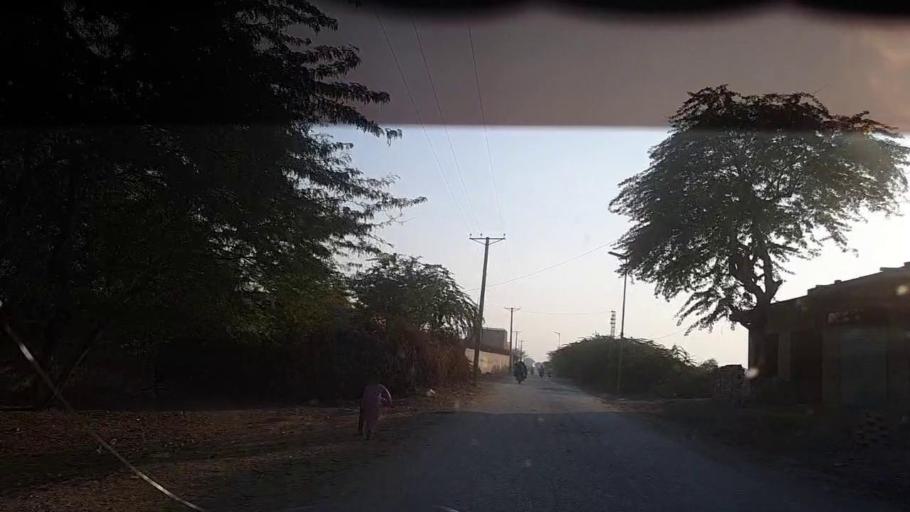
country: PK
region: Sindh
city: Ranipur
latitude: 27.2791
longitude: 68.5153
